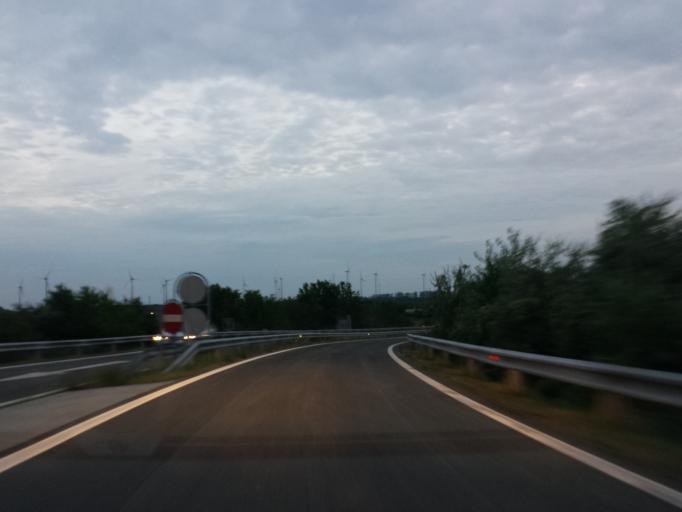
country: AT
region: Lower Austria
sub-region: Politischer Bezirk Baden
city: Ebreichsdorf
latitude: 47.9635
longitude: 16.3682
